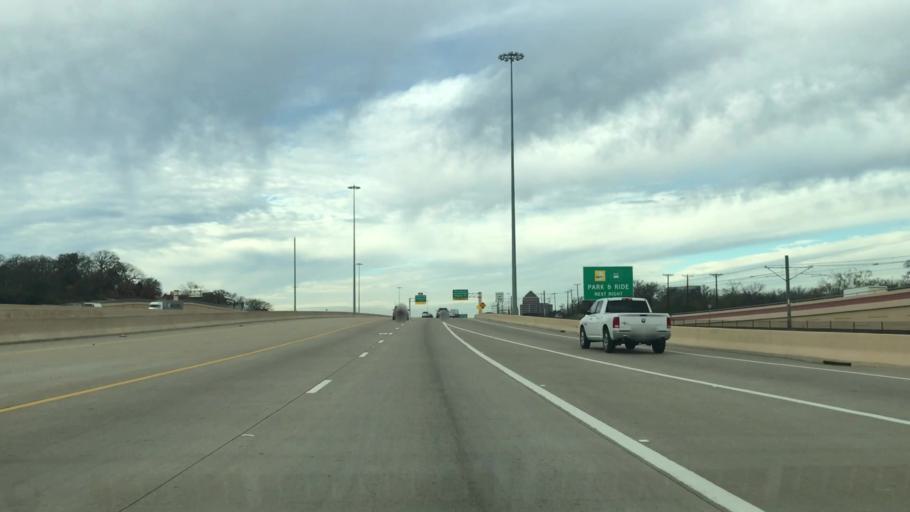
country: US
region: Texas
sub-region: Dallas County
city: Irving
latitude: 32.8500
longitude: -96.9174
